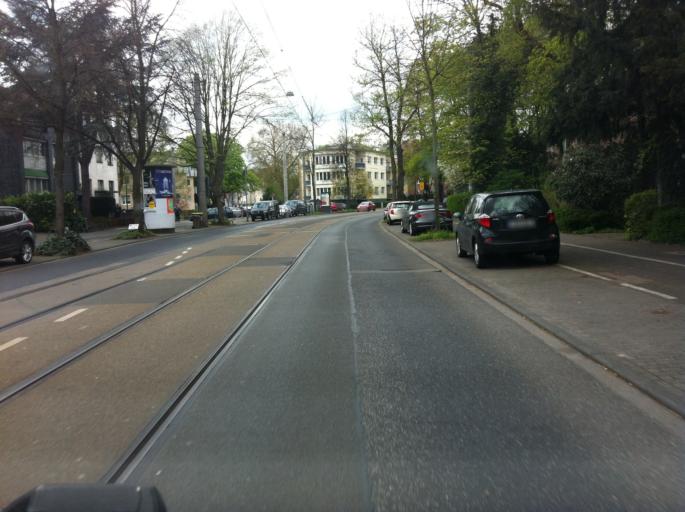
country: DE
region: North Rhine-Westphalia
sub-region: Regierungsbezirk Koln
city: Neustadt/Sued
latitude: 50.9271
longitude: 6.9070
